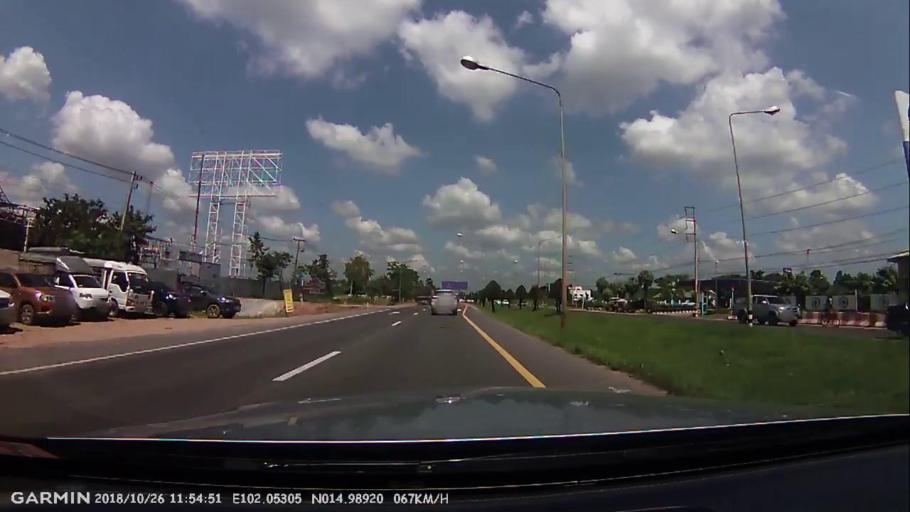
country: TH
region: Nakhon Ratchasima
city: Nakhon Ratchasima
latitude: 14.9893
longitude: 102.0531
